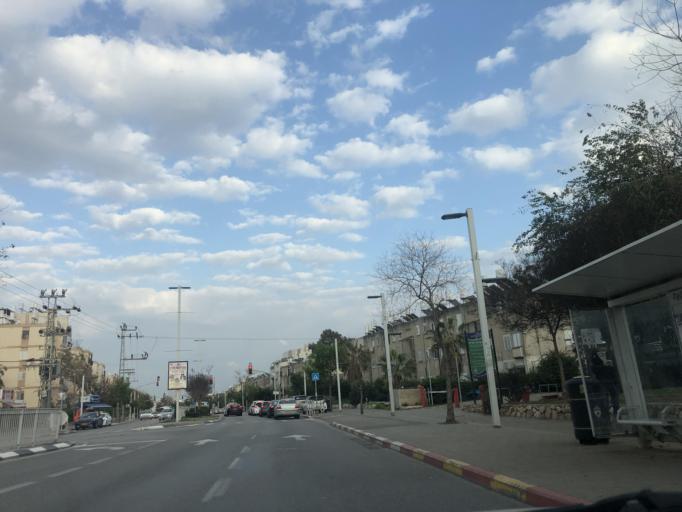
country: IL
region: Tel Aviv
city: Bat Yam
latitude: 32.0234
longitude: 34.7571
